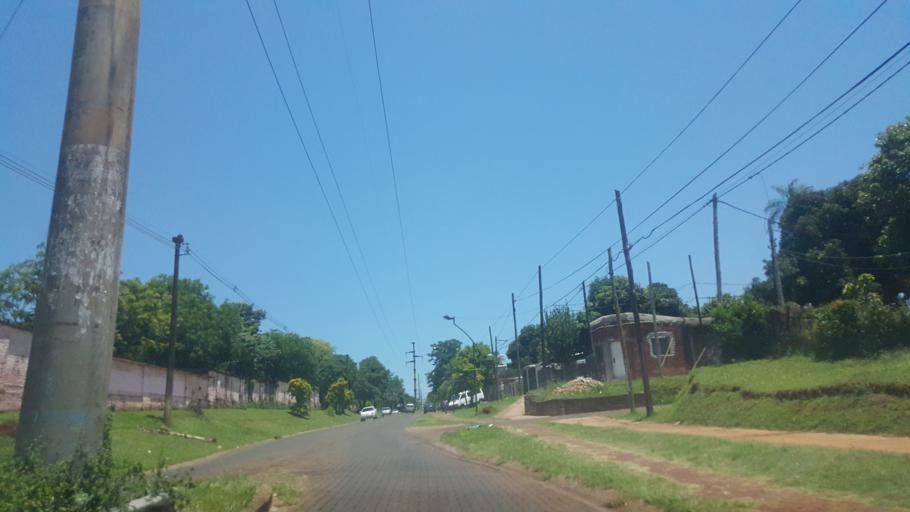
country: AR
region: Misiones
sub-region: Departamento de Capital
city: Posadas
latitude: -27.3807
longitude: -55.9146
